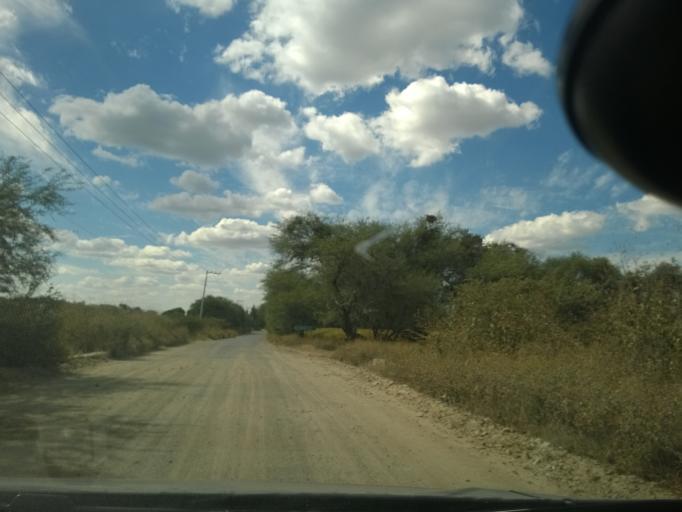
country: MX
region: Guanajuato
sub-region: Leon
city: Plan Guanajuato (La Sandia)
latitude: 20.9052
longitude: -101.6348
